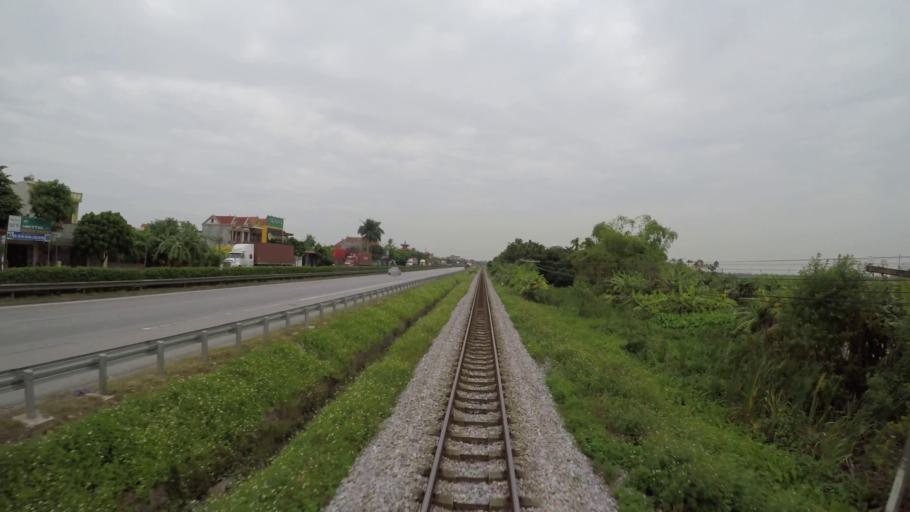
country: VN
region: Hai Duong
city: Phu Thai
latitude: 20.9694
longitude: 106.4464
